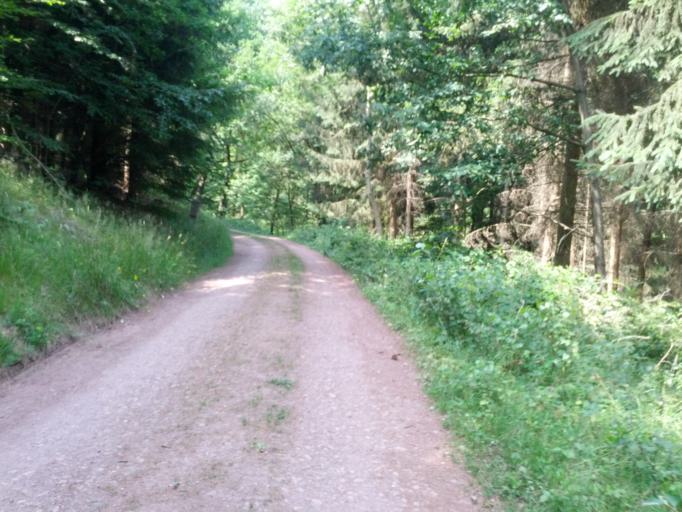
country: DE
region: Thuringia
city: Eisenach
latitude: 50.9522
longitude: 10.3452
